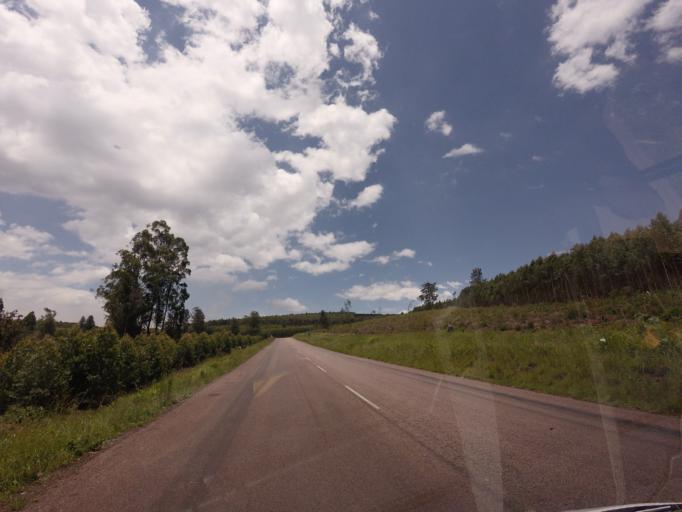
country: ZA
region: Mpumalanga
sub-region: Ehlanzeni District
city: Graksop
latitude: -25.0763
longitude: 30.7991
